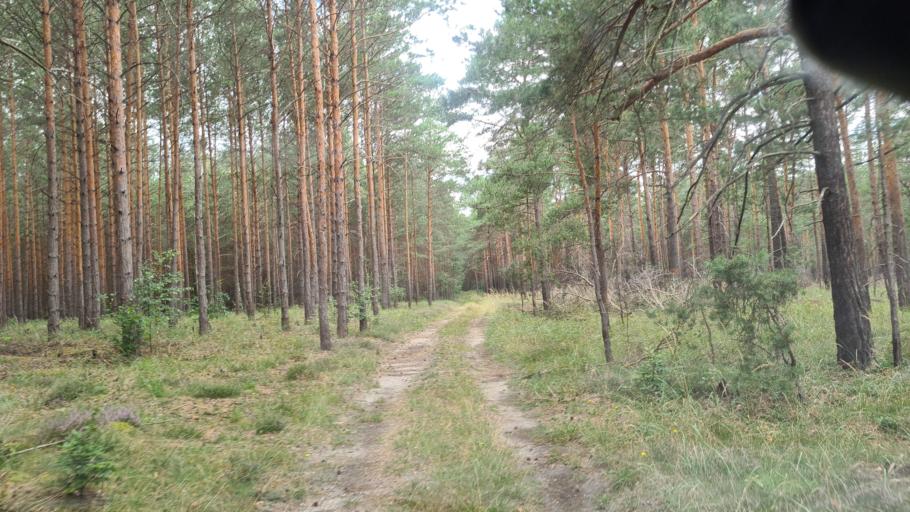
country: DE
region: Brandenburg
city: Sallgast
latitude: 51.5848
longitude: 13.8946
